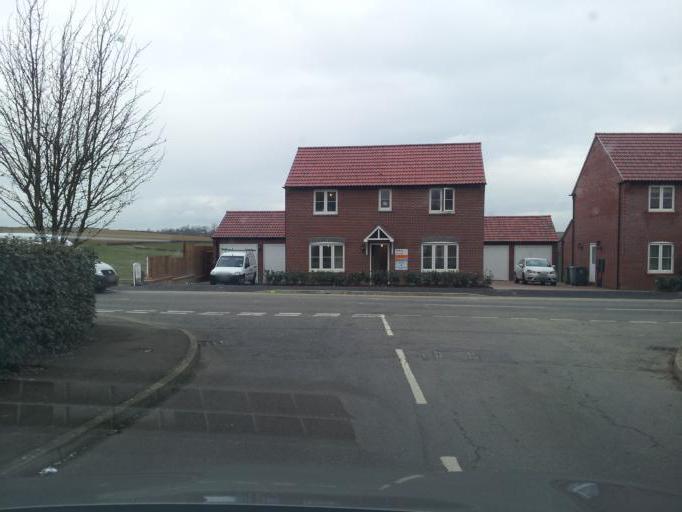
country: GB
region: England
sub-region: Lincolnshire
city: Great Gonerby
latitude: 52.9189
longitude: -0.6621
